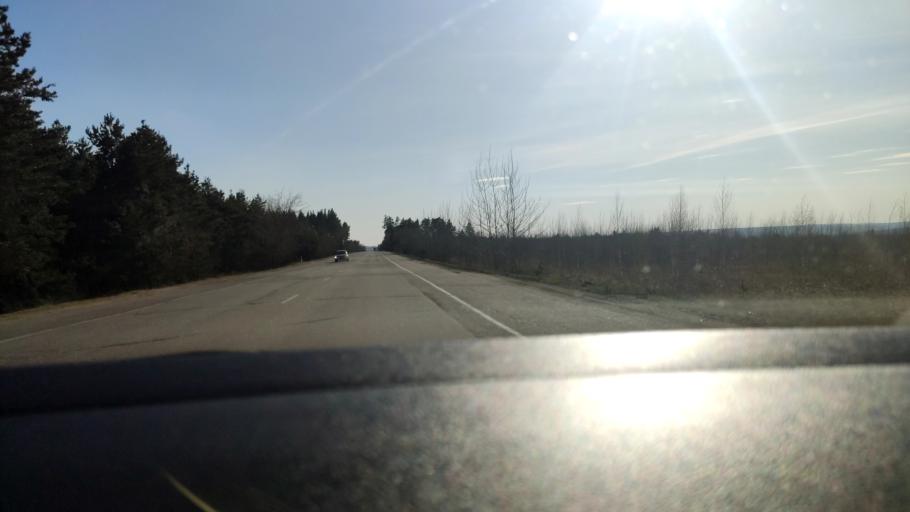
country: RU
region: Voronezj
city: Kolodeznyy
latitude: 51.3681
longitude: 39.2002
